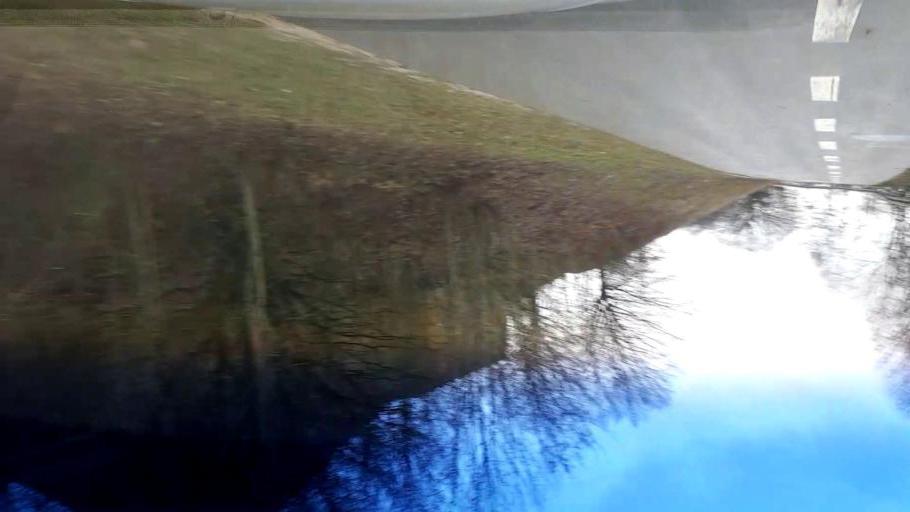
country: DE
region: Bavaria
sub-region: Upper Franconia
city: Schesslitz
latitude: 49.9555
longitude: 11.0484
